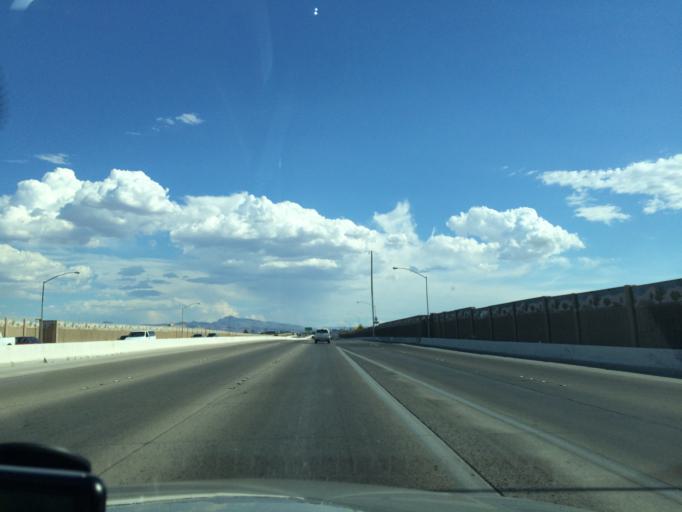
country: US
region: Nevada
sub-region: Clark County
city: Winchester
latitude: 36.1531
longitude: -115.0917
